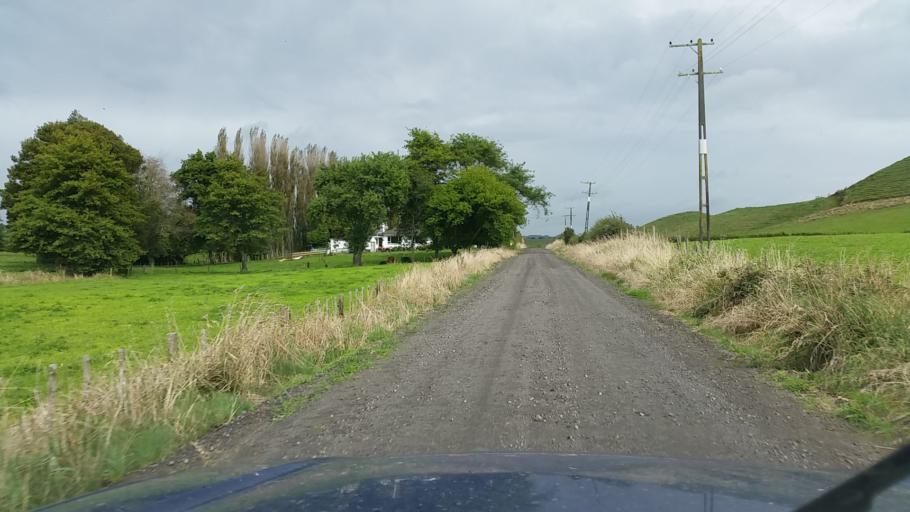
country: NZ
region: Taranaki
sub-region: South Taranaki District
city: Eltham
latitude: -39.3403
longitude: 174.4237
